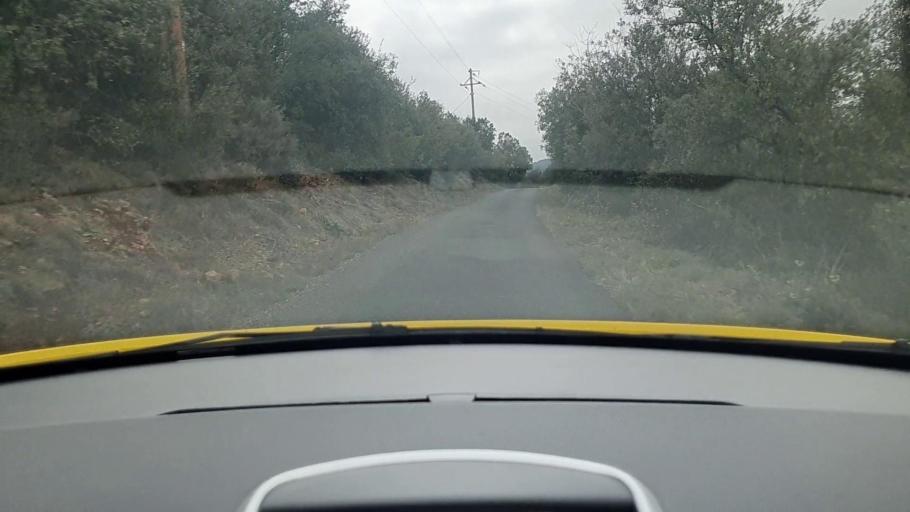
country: FR
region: Languedoc-Roussillon
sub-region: Departement du Gard
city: Saint-Florent-sur-Auzonnet
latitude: 44.2635
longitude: 4.1239
